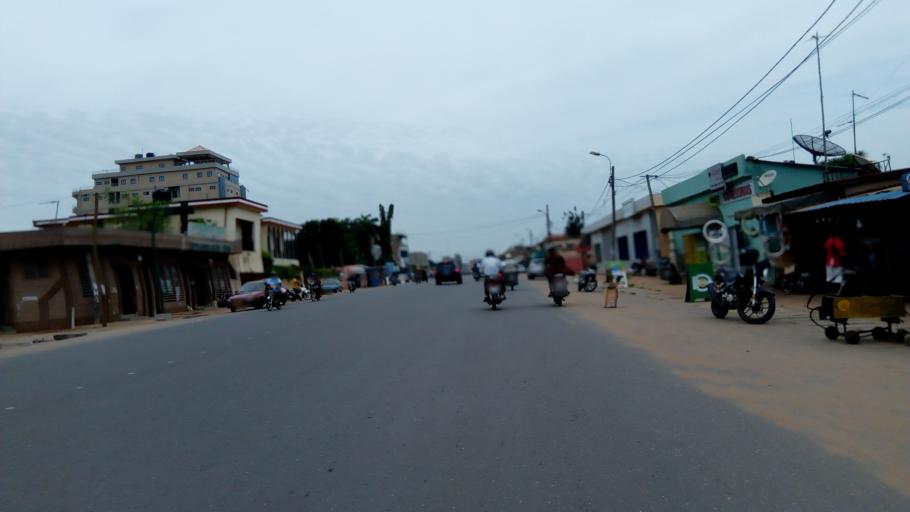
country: TG
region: Maritime
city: Lome
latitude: 6.1568
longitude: 1.2332
